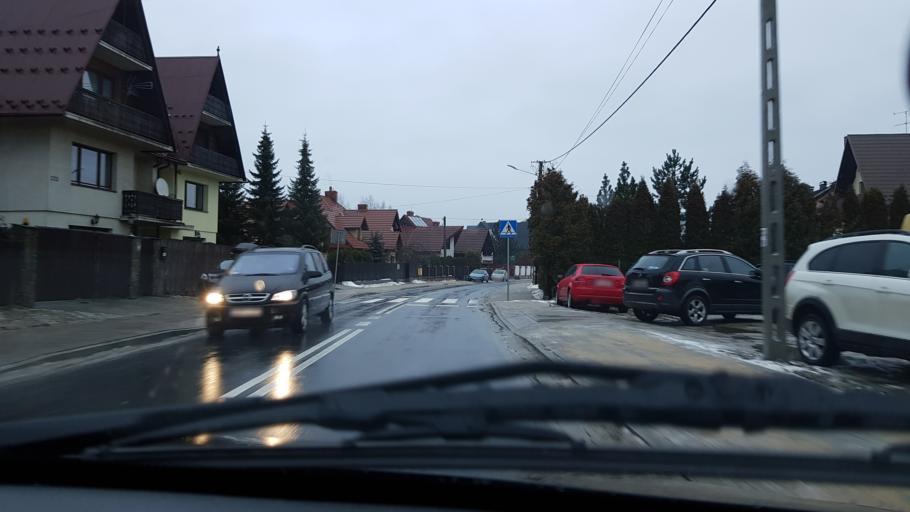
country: PL
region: Lesser Poland Voivodeship
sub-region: Powiat nowotarski
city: Ludzmierz
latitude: 49.4855
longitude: 19.9971
